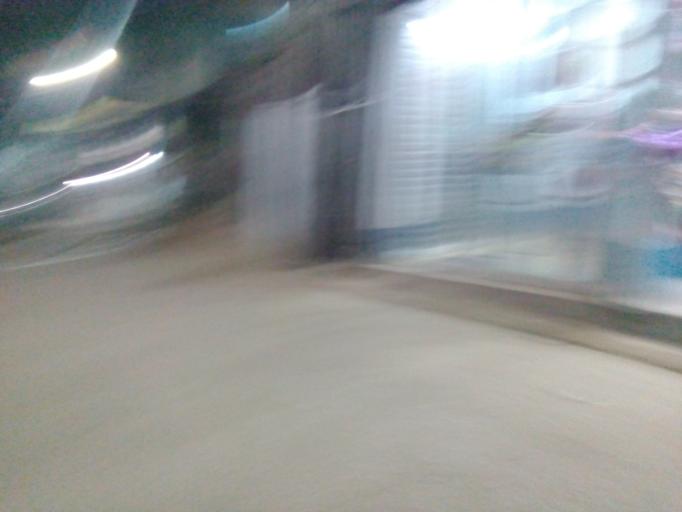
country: BD
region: Dhaka
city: Paltan
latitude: 23.7436
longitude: 90.4219
